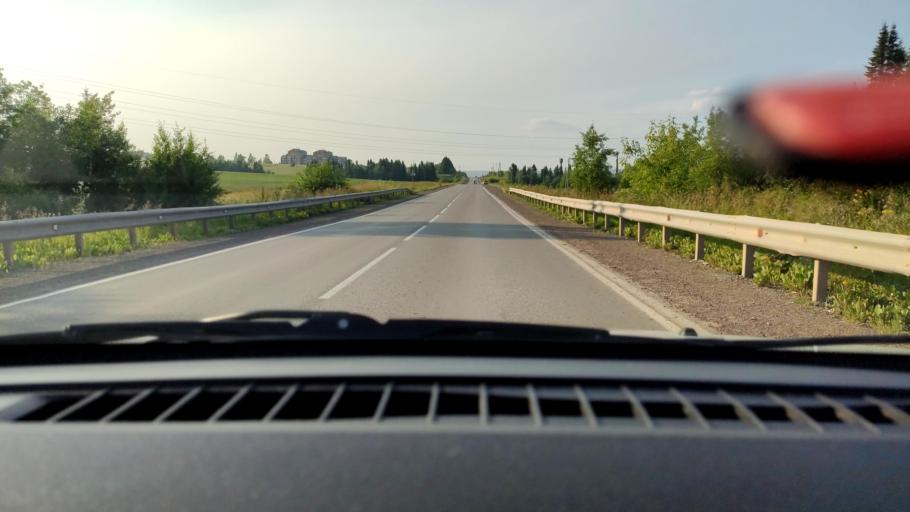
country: RU
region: Perm
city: Lobanovo
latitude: 57.8526
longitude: 56.2962
